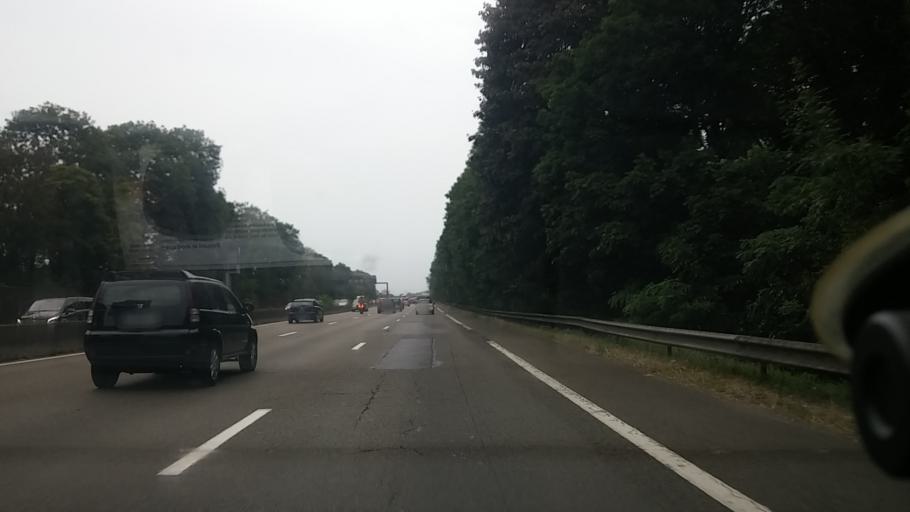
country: FR
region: Ile-de-France
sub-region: Departement des Hauts-de-Seine
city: Marnes-la-Coquette
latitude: 48.8339
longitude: 2.1662
